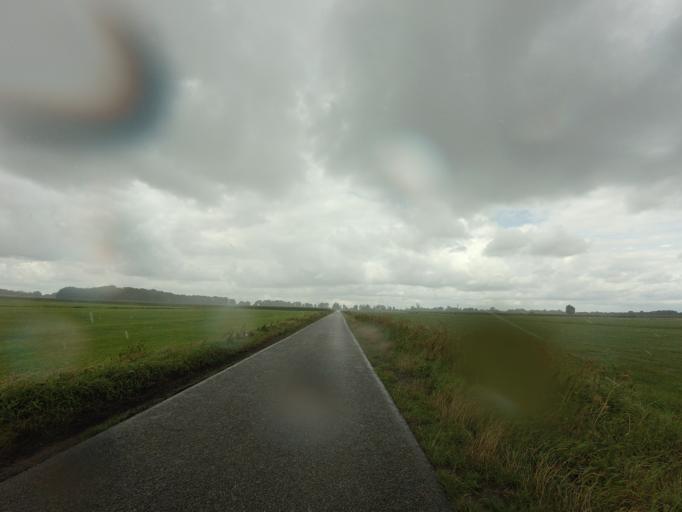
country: NL
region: Overijssel
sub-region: Gemeente Steenwijkerland
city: Wanneperveen
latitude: 52.7157
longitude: 6.1593
